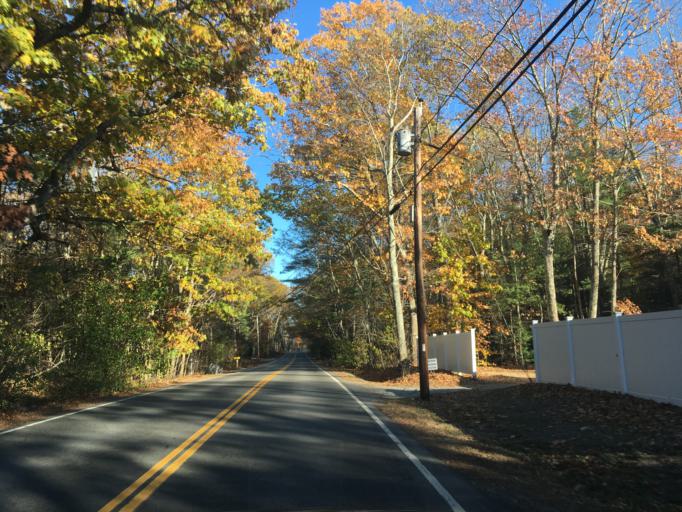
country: US
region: New Hampshire
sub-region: Rockingham County
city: Stratham Station
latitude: 43.0387
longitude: -70.9115
